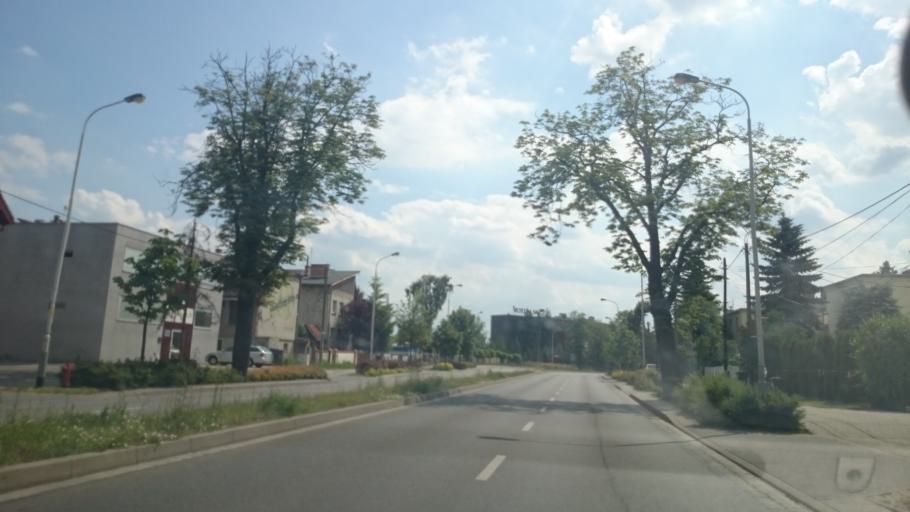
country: PL
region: Lower Silesian Voivodeship
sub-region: Powiat wroclawski
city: Wroclaw
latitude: 51.0669
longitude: 17.0079
